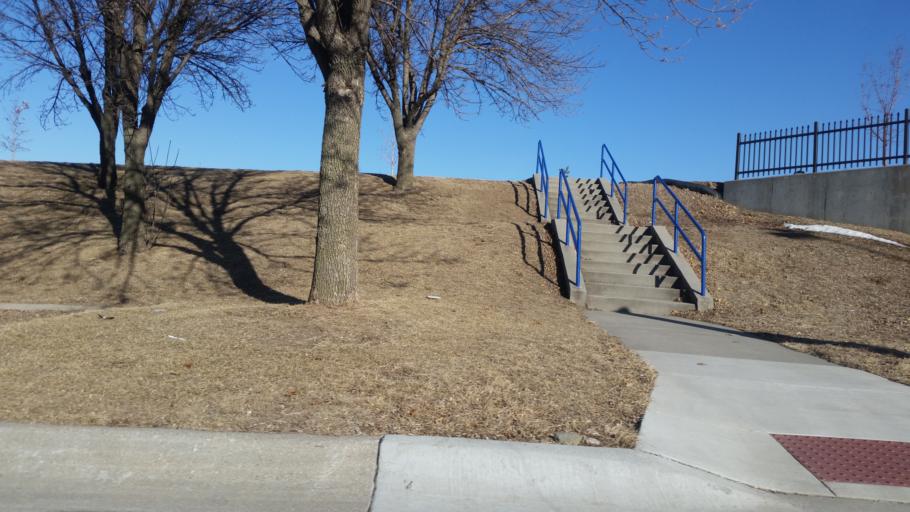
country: US
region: Nebraska
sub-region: Douglas County
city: Omaha
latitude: 41.2255
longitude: -95.9328
